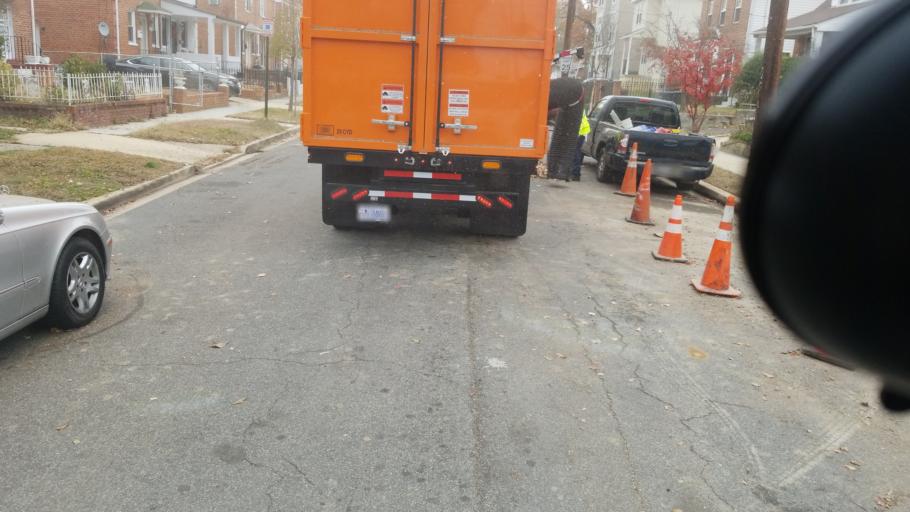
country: US
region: Maryland
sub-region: Prince George's County
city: Capitol Heights
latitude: 38.8842
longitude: -76.9220
